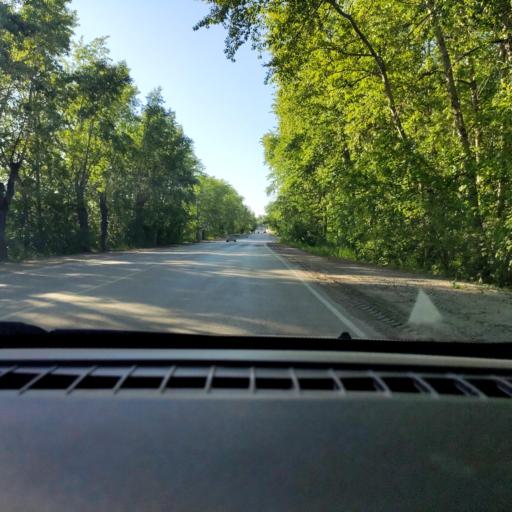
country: RU
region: Perm
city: Krasnokamsk
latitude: 58.0664
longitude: 55.7964
